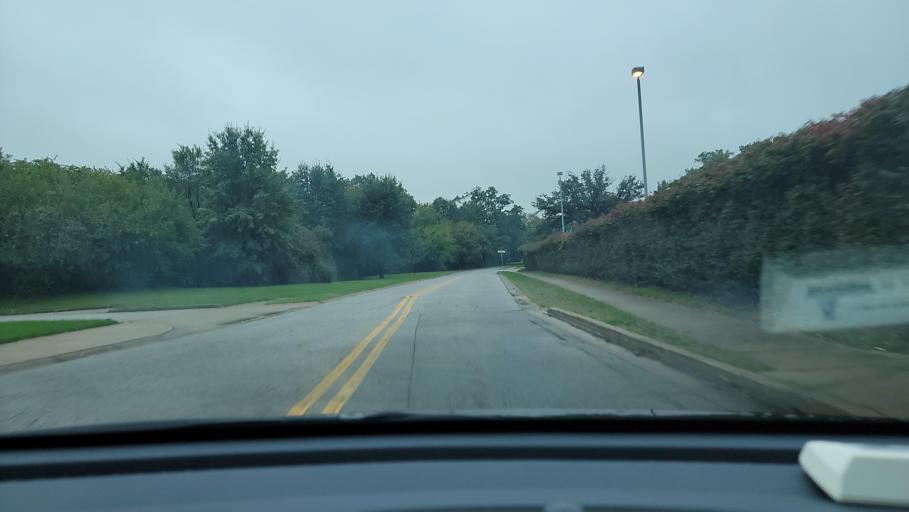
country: US
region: Indiana
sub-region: Porter County
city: Portage
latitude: 41.5736
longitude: -87.1812
